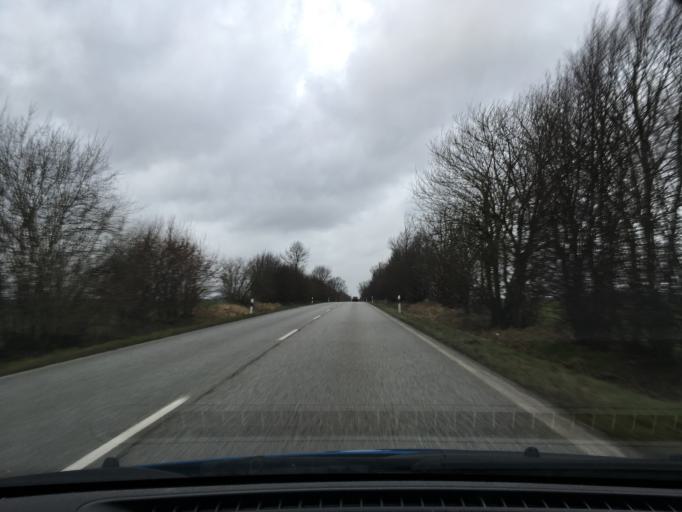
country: DE
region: Schleswig-Holstein
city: Wangelau
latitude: 53.4634
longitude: 10.5437
